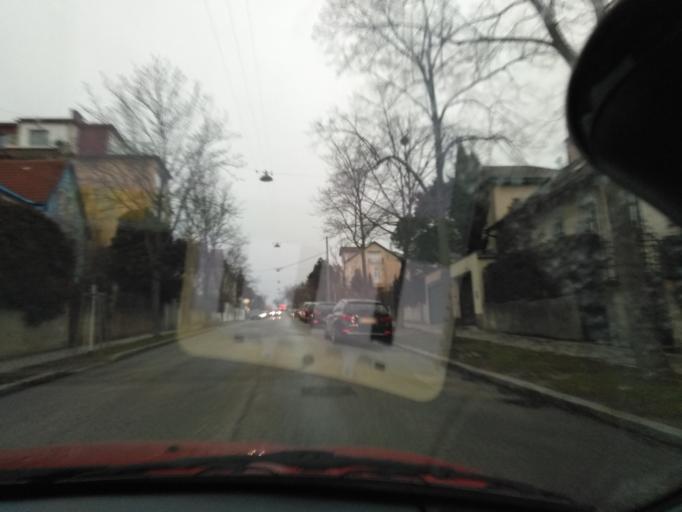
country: AT
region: Vienna
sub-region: Wien Stadt
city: Vienna
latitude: 48.2291
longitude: 16.3228
